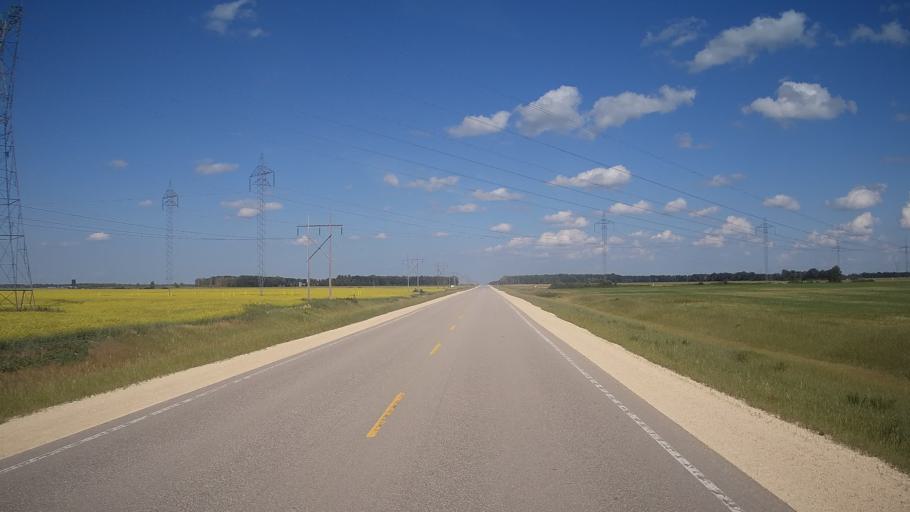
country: CA
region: Manitoba
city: Stonewall
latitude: 50.1227
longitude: -97.4932
